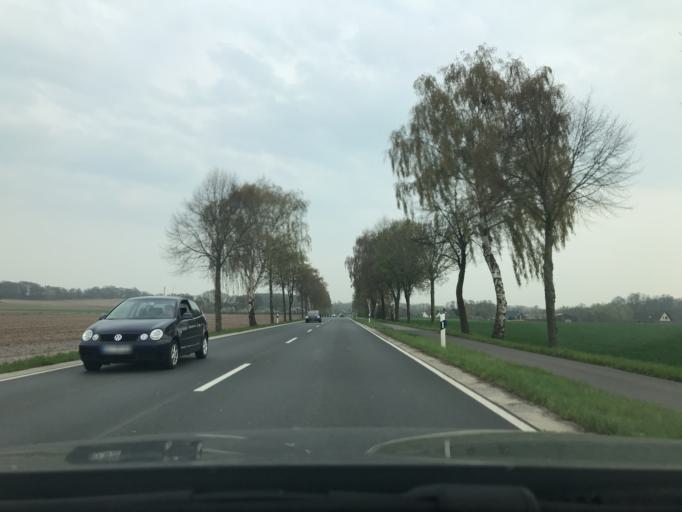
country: DE
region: North Rhine-Westphalia
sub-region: Regierungsbezirk Dusseldorf
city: Rheurdt
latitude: 51.4178
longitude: 6.4688
